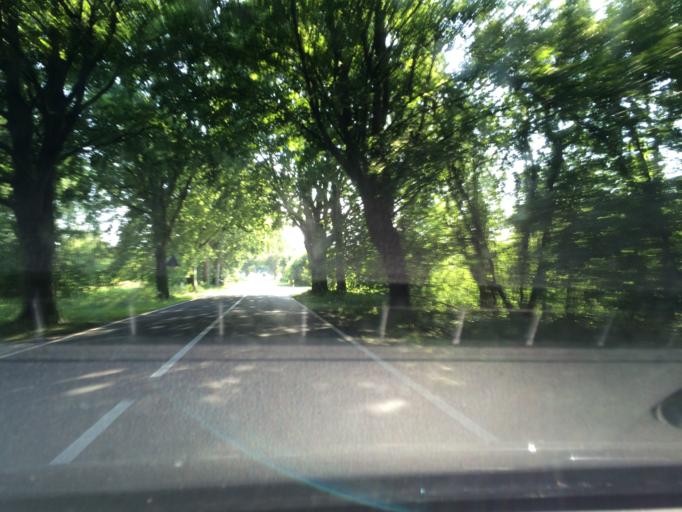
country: DE
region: Mecklenburg-Vorpommern
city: Ostseebad Binz
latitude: 54.4167
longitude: 13.5412
